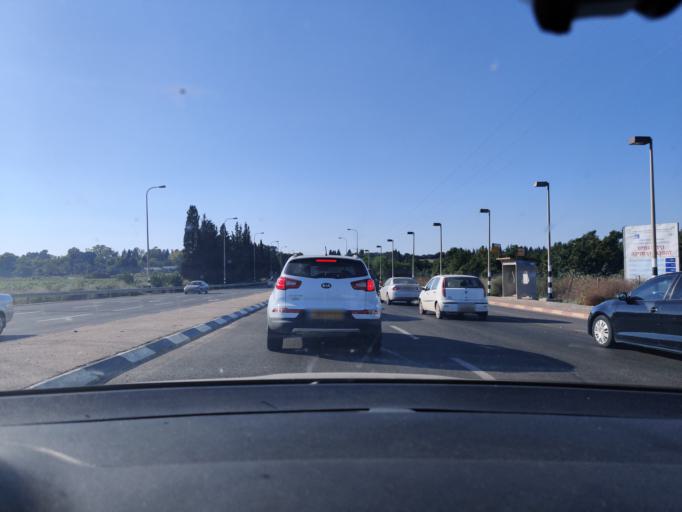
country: PS
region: West Bank
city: Nazlat `Isa
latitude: 32.4441
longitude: 35.0219
